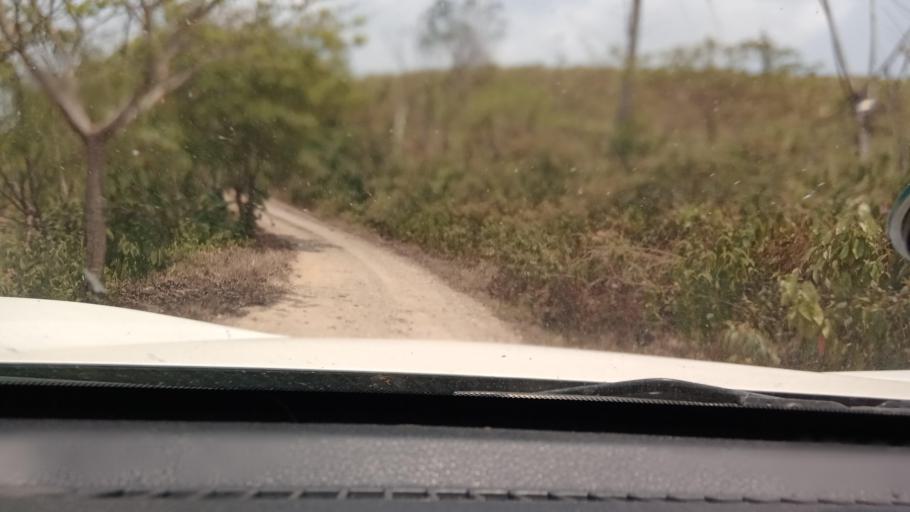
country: MX
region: Tabasco
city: Chontalpa
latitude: 17.5596
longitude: -93.7249
